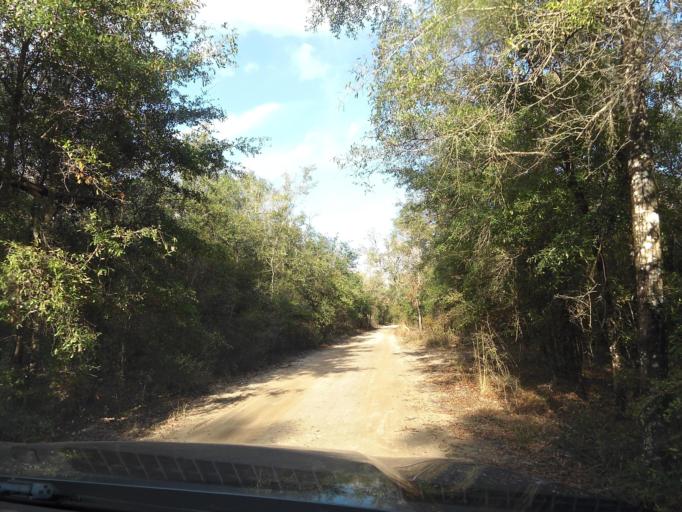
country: US
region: Florida
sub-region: Clay County
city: Middleburg
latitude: 30.1382
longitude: -81.9391
